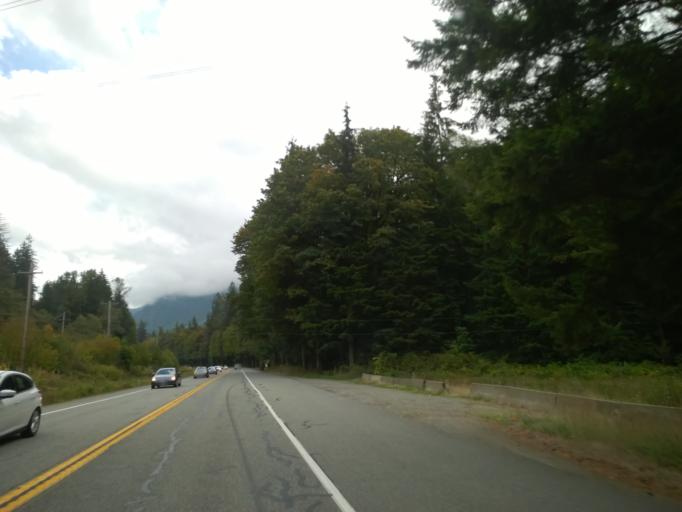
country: US
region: Washington
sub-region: Snohomish County
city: Gold Bar
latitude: 47.7833
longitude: -121.4975
